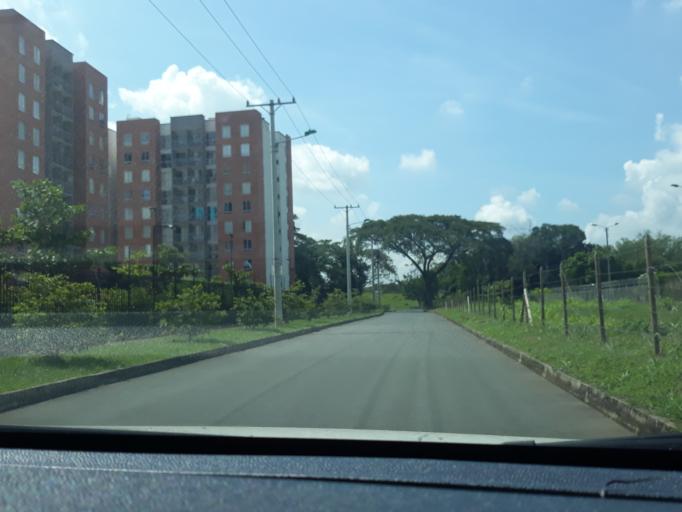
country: CO
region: Valle del Cauca
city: Cali
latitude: 3.3664
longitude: -76.5118
